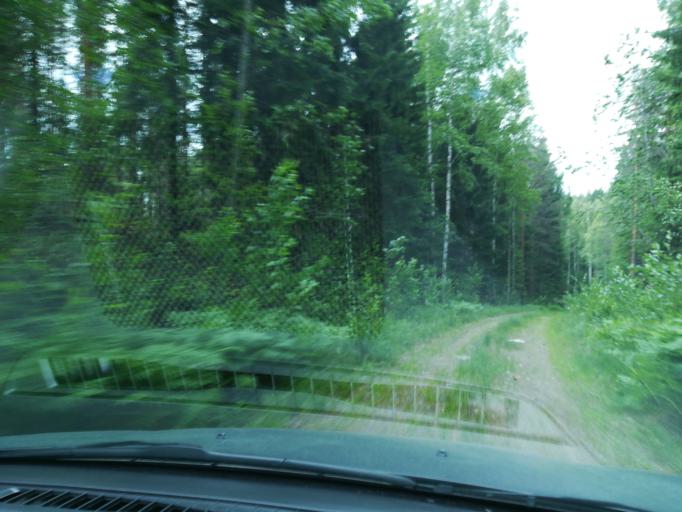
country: FI
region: South Karelia
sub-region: Lappeenranta
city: Savitaipale
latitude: 61.3054
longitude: 27.6183
